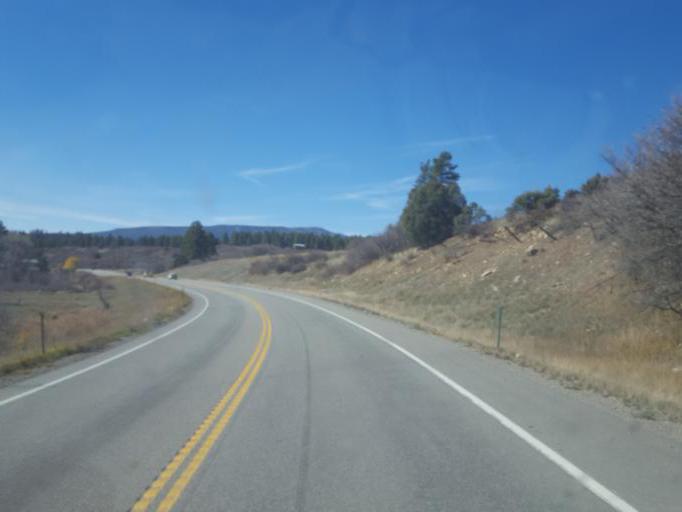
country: US
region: Colorado
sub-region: Archuleta County
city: Pagosa Springs
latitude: 37.2407
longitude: -107.1406
